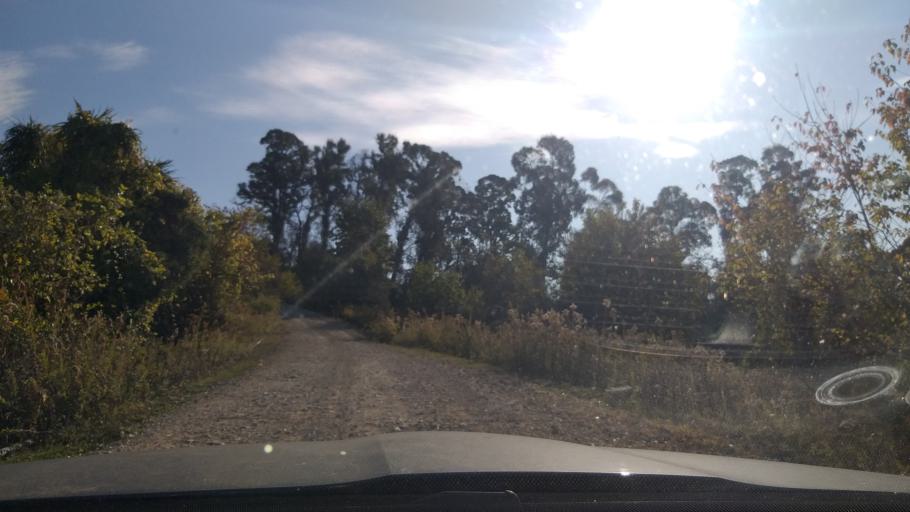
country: GE
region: Abkhazia
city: Stantsiya Novyy Afon
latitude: 43.0489
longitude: 40.9033
